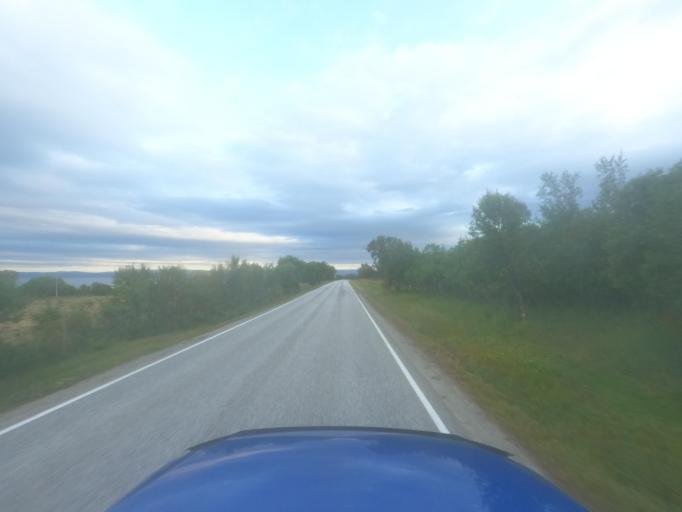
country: NO
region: Finnmark Fylke
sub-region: Porsanger
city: Lakselv
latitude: 70.4634
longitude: 25.2250
